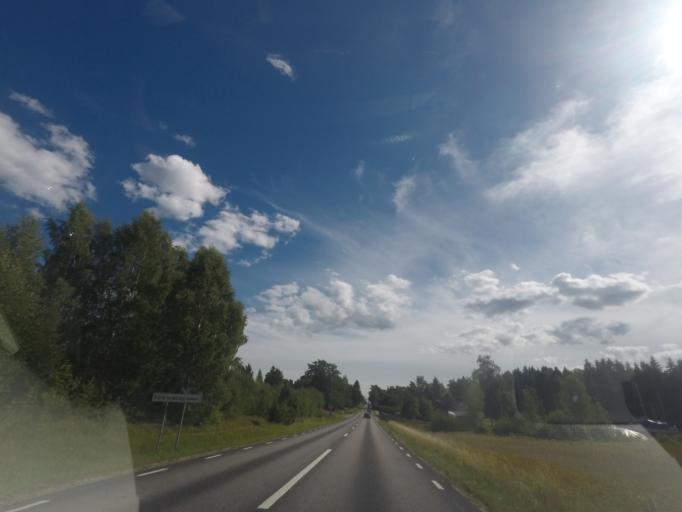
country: SE
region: Stockholm
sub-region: Norrtalje Kommun
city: Arno
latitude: 59.9996
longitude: 18.8015
